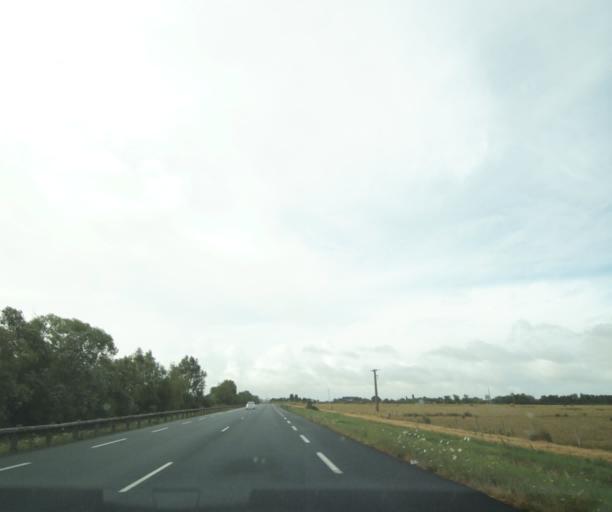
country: FR
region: Pays de la Loire
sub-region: Departement de la Vendee
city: Champagne-les-Marais
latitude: 46.3841
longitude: -1.0925
